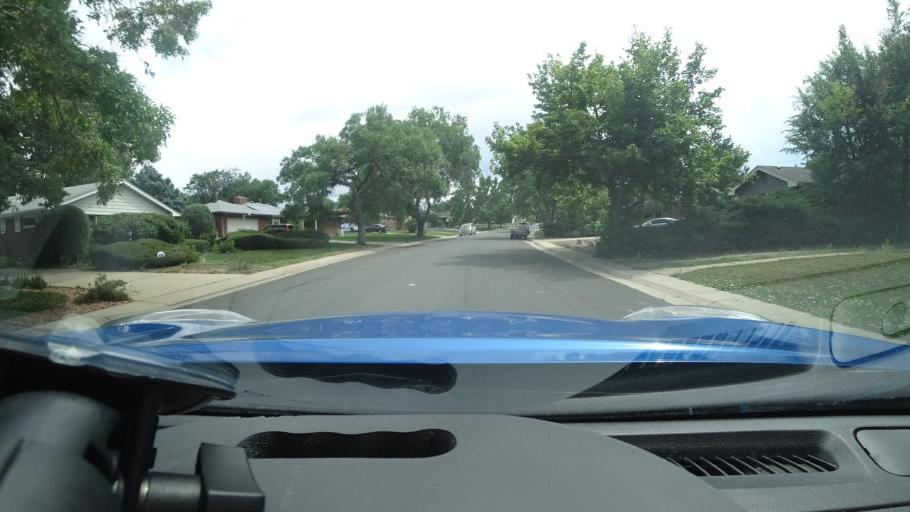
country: US
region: Colorado
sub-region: Adams County
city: Aurora
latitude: 39.7234
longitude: -104.8333
